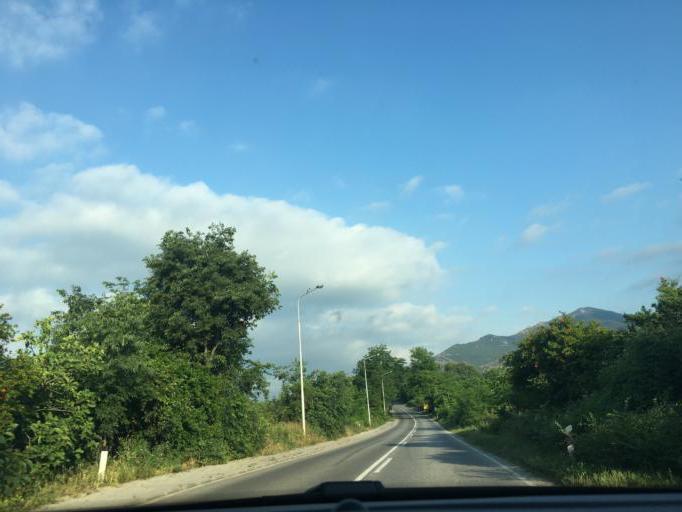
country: MK
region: Valandovo
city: Valandovo
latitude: 41.3174
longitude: 22.5837
